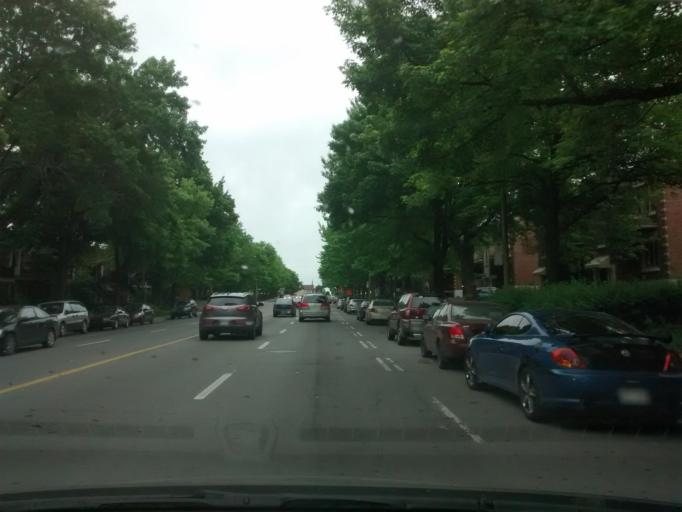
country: CA
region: Quebec
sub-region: Montreal
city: Saint-Leonard
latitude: 45.5549
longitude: -73.5857
